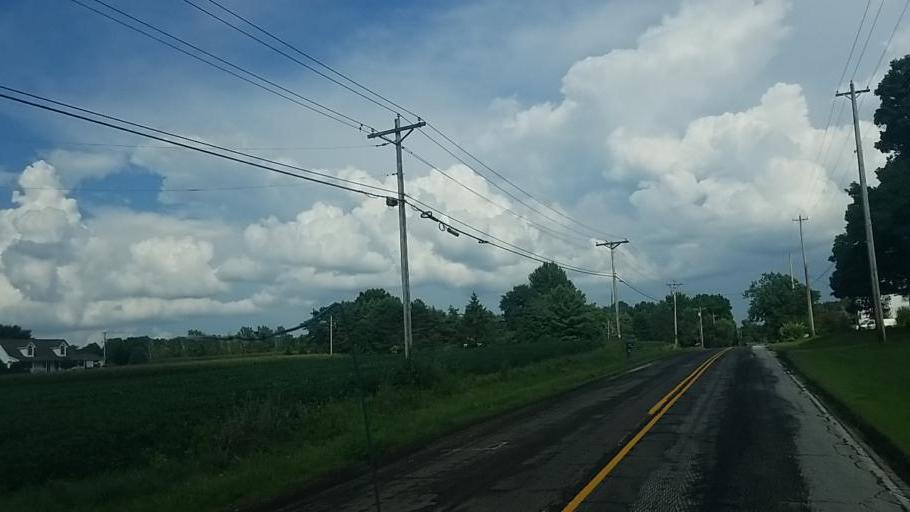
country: US
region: Ohio
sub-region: Medina County
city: Lodi
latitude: 41.0263
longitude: -81.9828
